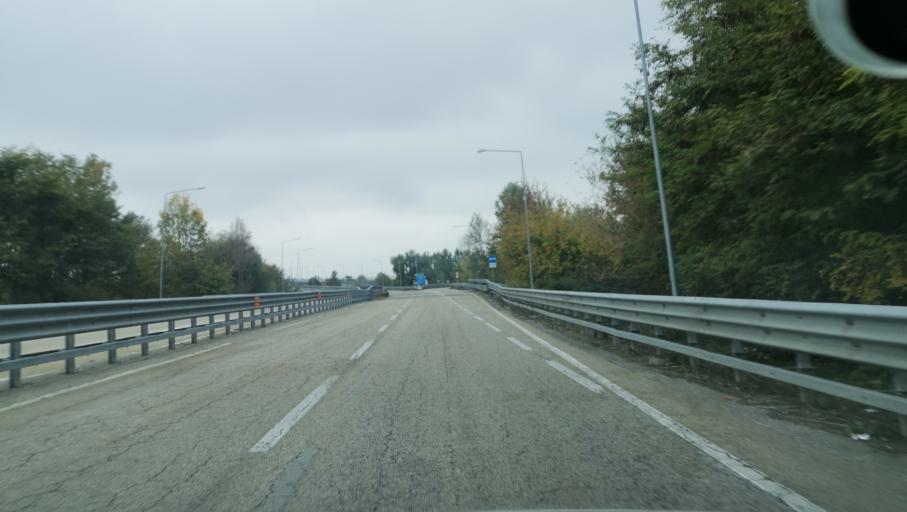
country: IT
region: Piedmont
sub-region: Provincia di Torino
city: Brandizzo
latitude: 45.1638
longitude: 7.8207
